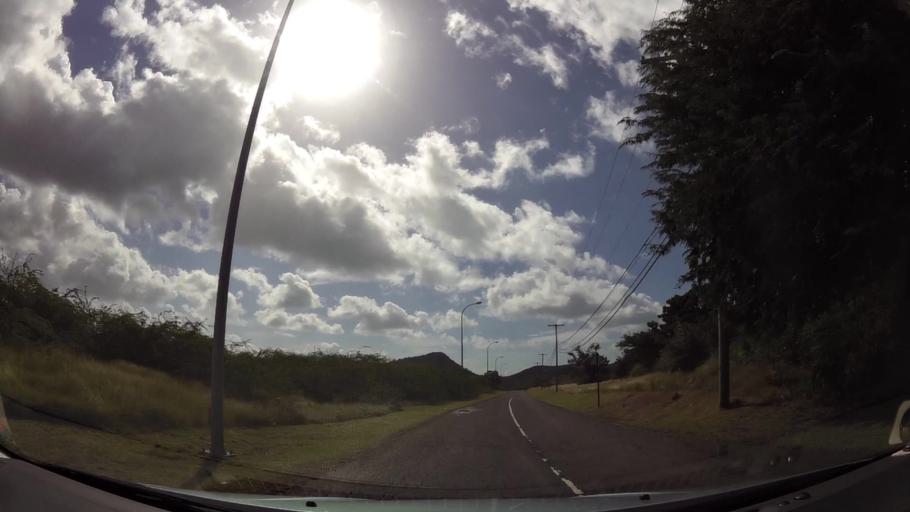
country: AG
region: Saint John
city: Saint John's
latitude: 17.1173
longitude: -61.8696
